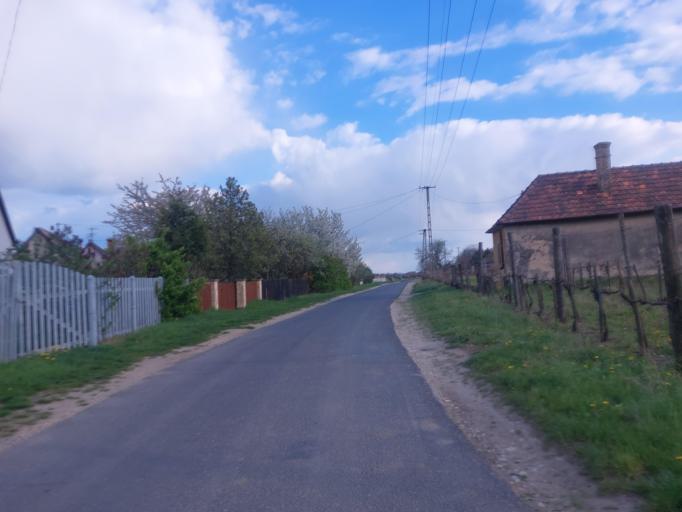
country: HU
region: Veszprem
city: Devecser
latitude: 47.1511
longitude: 17.3841
